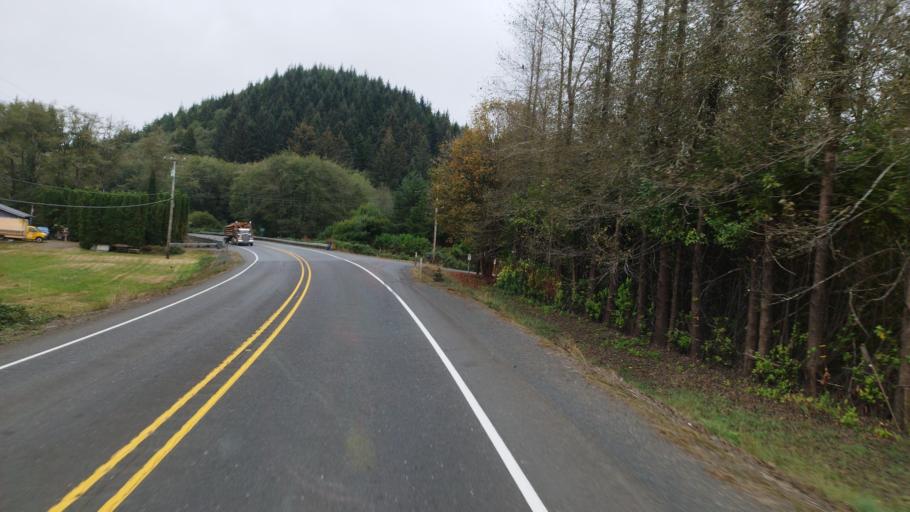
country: US
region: Oregon
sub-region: Clatsop County
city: Cannon Beach
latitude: 45.9202
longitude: -123.8952
